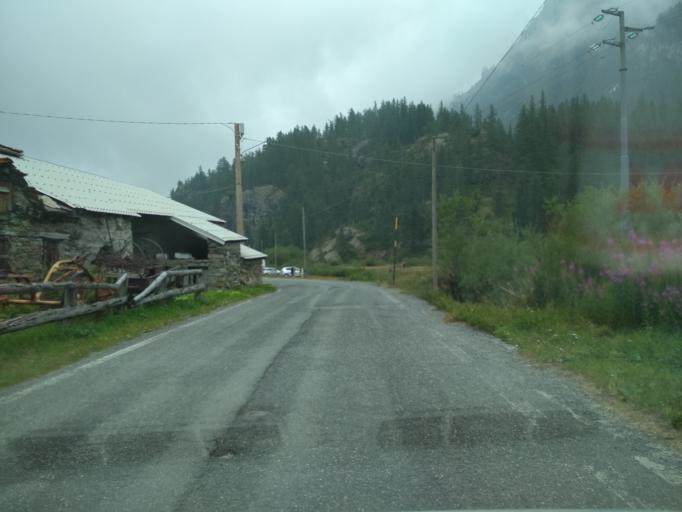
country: IT
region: Piedmont
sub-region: Provincia di Torino
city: Balme
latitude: 45.3035
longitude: 7.1770
